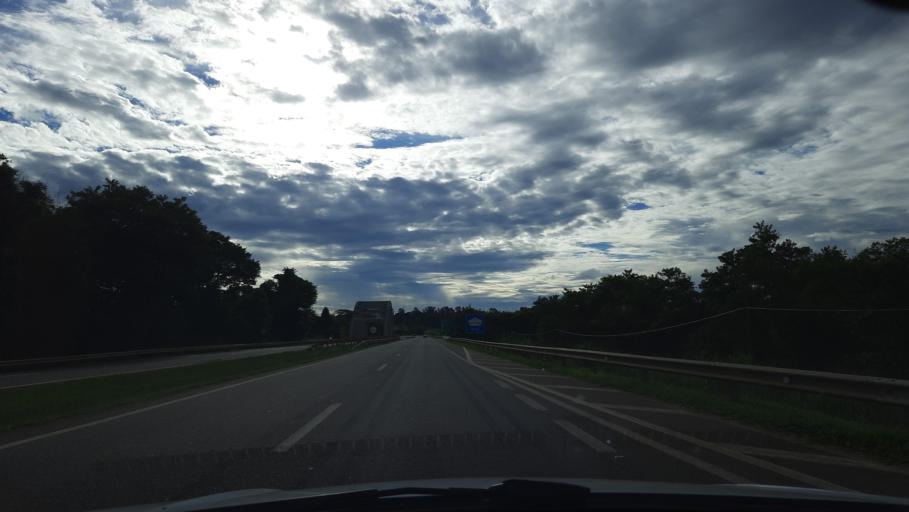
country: BR
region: Sao Paulo
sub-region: Sao Joao Da Boa Vista
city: Sao Joao da Boa Vista
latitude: -21.9925
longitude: -46.7962
